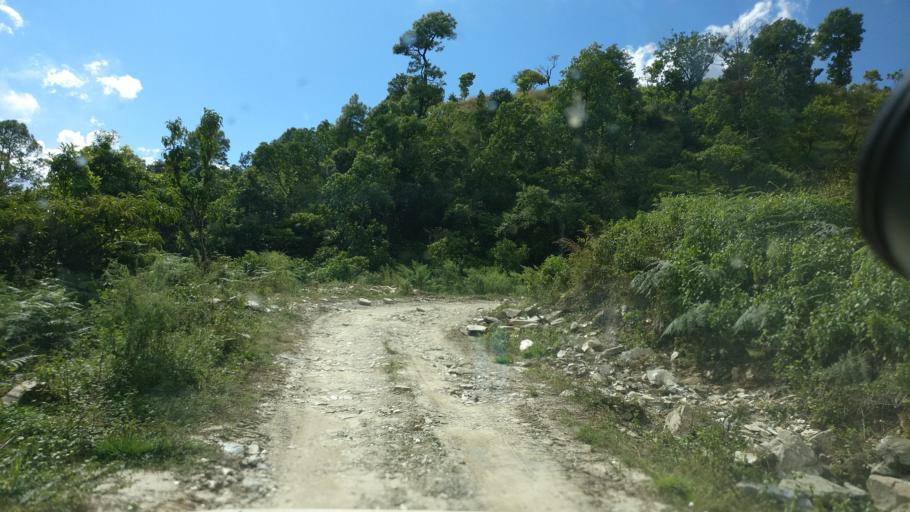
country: NP
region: Western Region
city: Baglung
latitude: 28.2766
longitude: 83.6410
